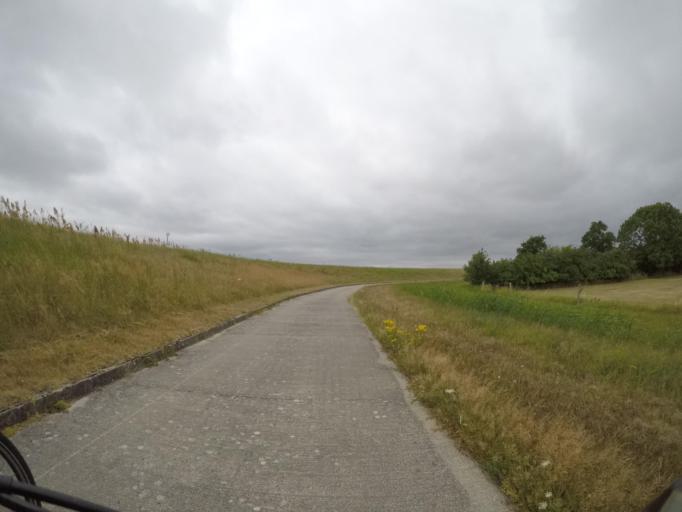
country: DE
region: Lower Saxony
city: Hitzacker
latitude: 53.1570
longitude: 11.0698
